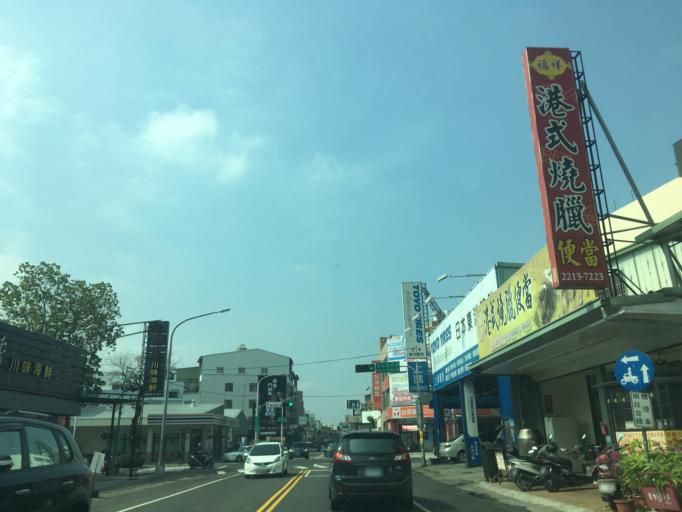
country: TW
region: Taiwan
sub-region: Taichung City
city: Taichung
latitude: 24.1432
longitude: 120.7088
